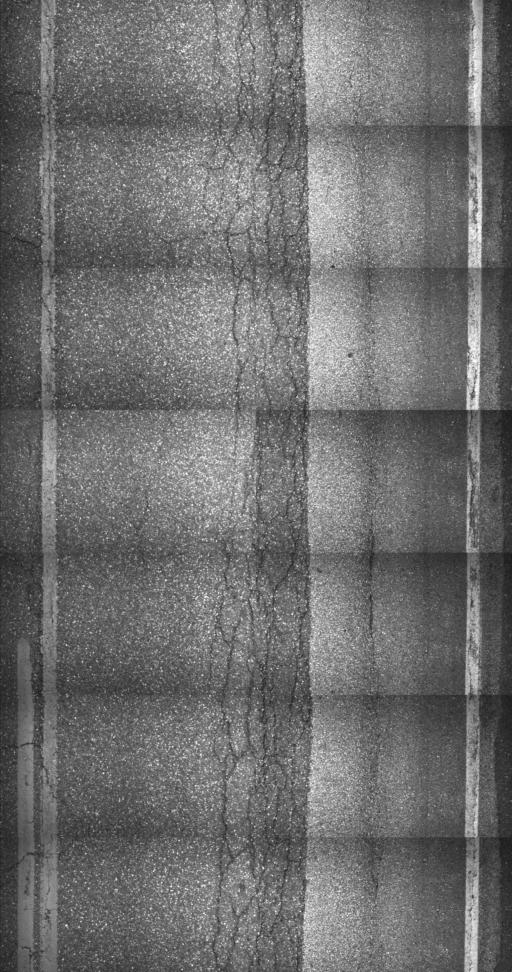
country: US
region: New York
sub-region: Essex County
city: Ticonderoga
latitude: 43.8174
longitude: -73.3060
